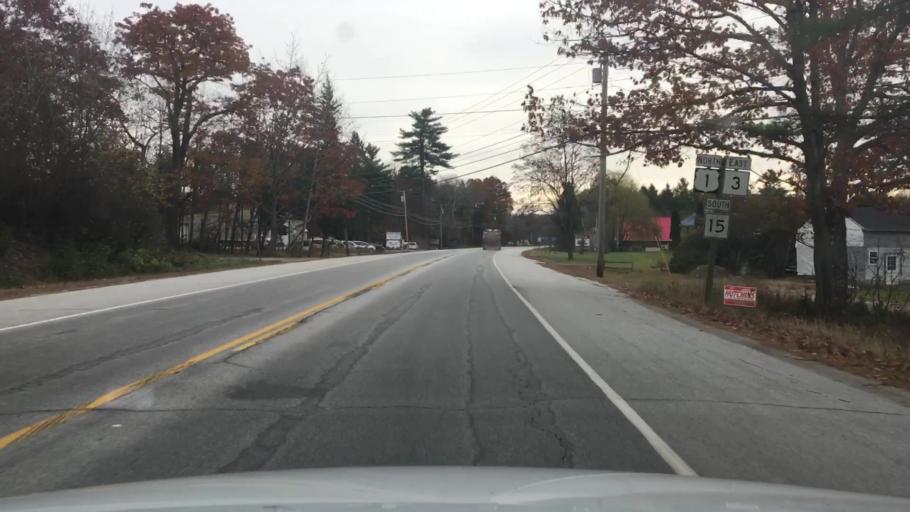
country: US
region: Maine
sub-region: Hancock County
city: Orland
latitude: 44.5668
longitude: -68.7191
